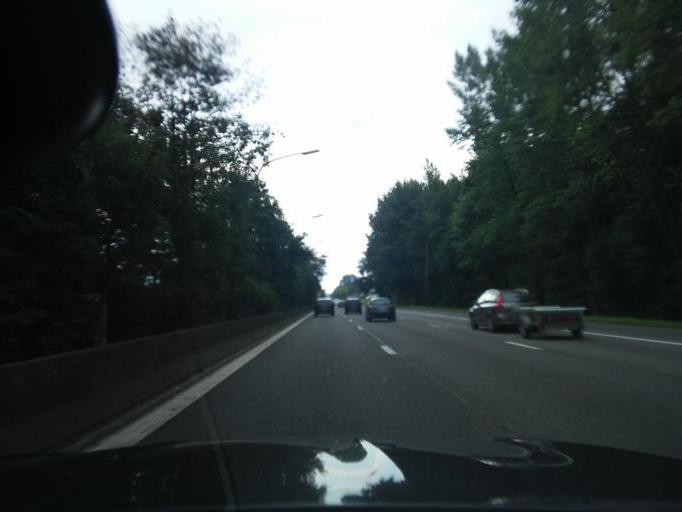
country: BE
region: Flanders
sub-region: Provincie Vlaams-Brabant
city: Londerzeel
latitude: 50.9861
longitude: 4.3159
